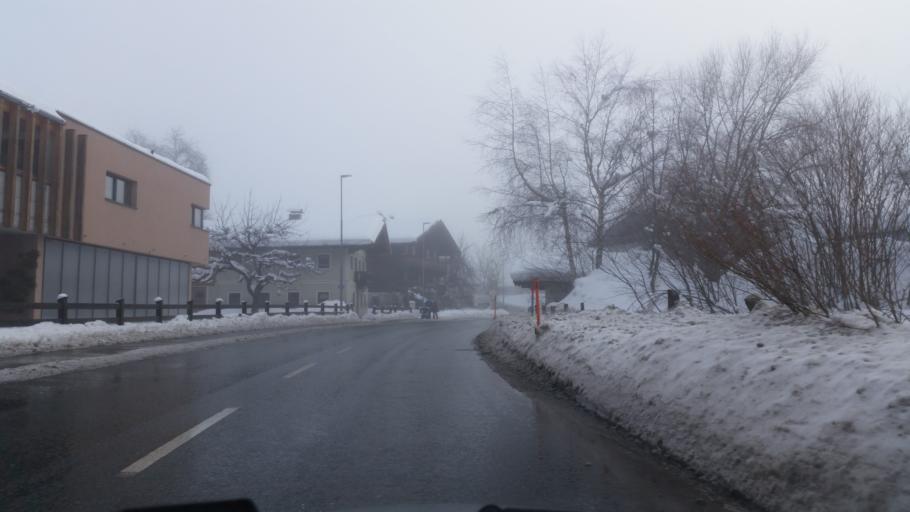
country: AT
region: Tyrol
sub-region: Politischer Bezirk Kitzbuhel
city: Sankt Johann in Tirol
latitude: 47.5203
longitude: 12.4358
